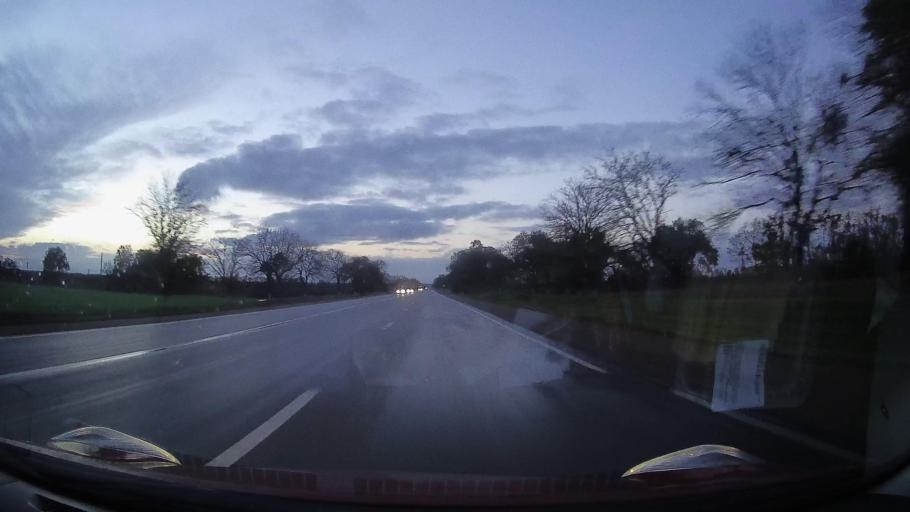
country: RU
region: Krasnodarskiy
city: Zavetnyy
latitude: 44.8964
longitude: 41.1946
